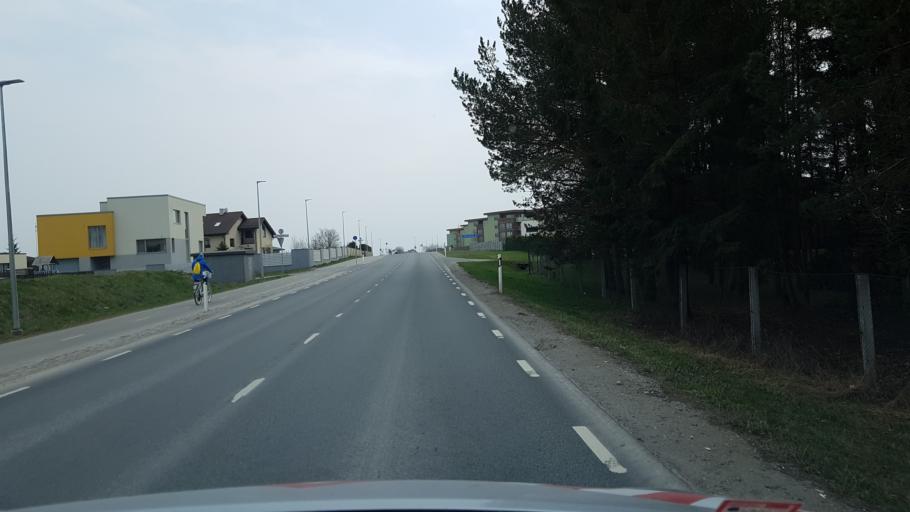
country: EE
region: Harju
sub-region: Tallinna linn
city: Tallinn
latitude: 59.3935
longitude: 24.7951
